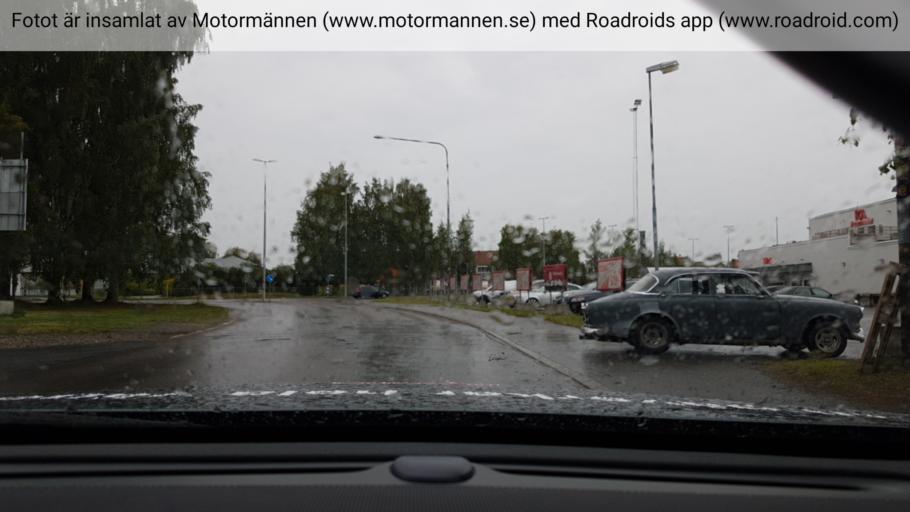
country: SE
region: Vaesterbotten
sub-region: Umea Kommun
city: Umea
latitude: 63.8183
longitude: 20.2468
